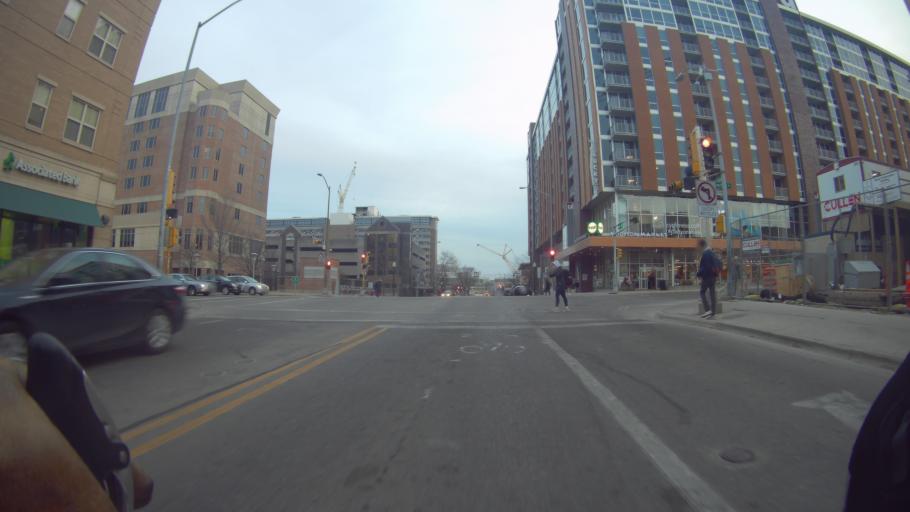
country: US
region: Wisconsin
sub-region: Dane County
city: Madison
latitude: 43.0738
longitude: -89.3974
